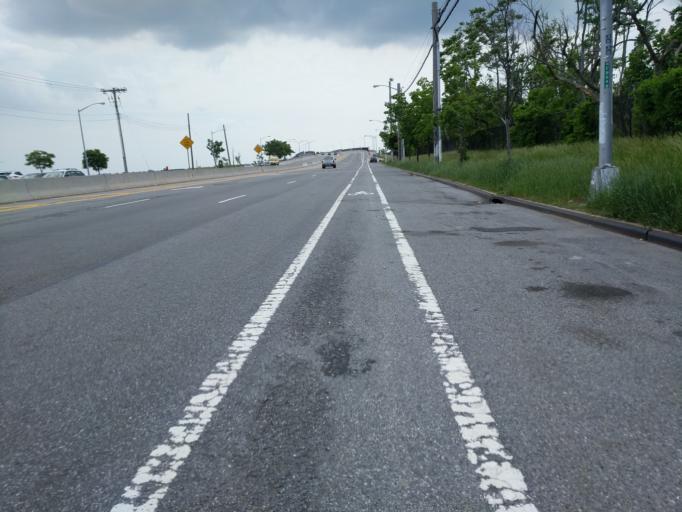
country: US
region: New York
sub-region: Queens County
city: Borough of Queens
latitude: 40.6486
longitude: -73.8374
